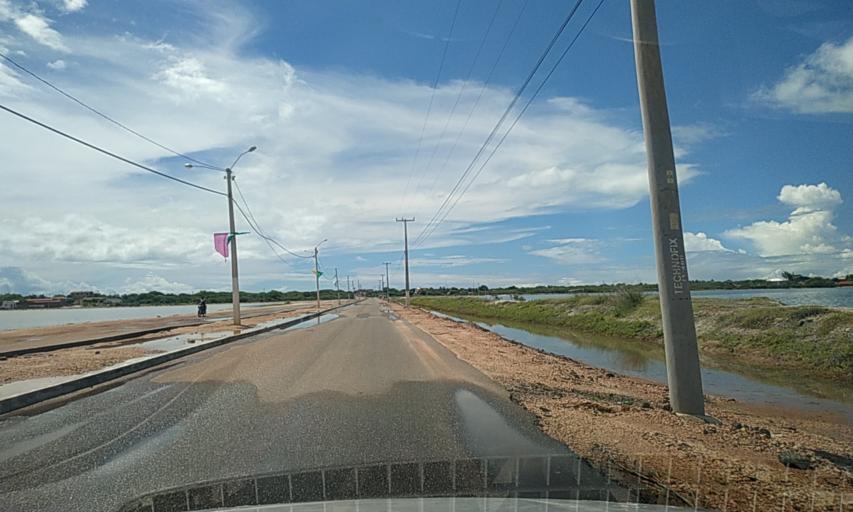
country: BR
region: Rio Grande do Norte
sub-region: Areia Branca
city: Areia Branca
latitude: -4.9387
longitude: -37.1130
